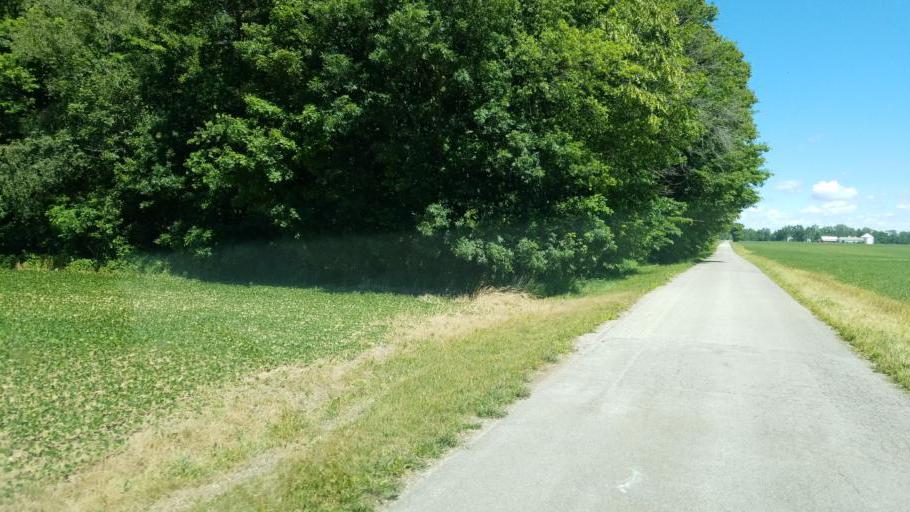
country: US
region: Ohio
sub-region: Morrow County
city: Cardington
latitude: 40.6215
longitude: -82.9427
